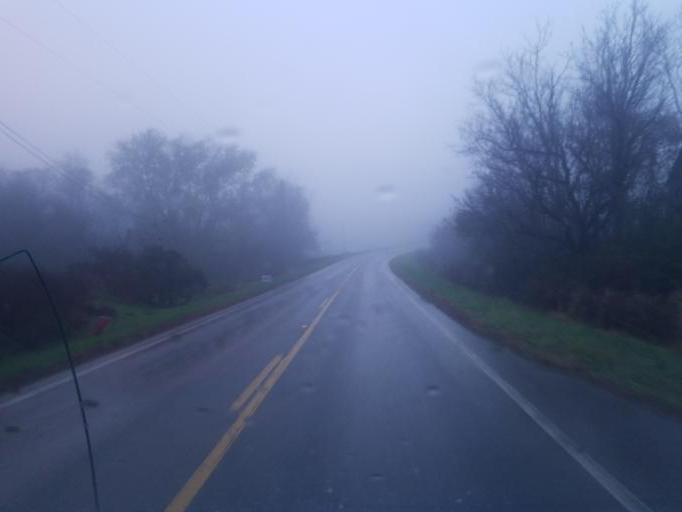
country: US
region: Ohio
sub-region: Morgan County
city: McConnelsville
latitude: 39.5037
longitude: -81.8559
